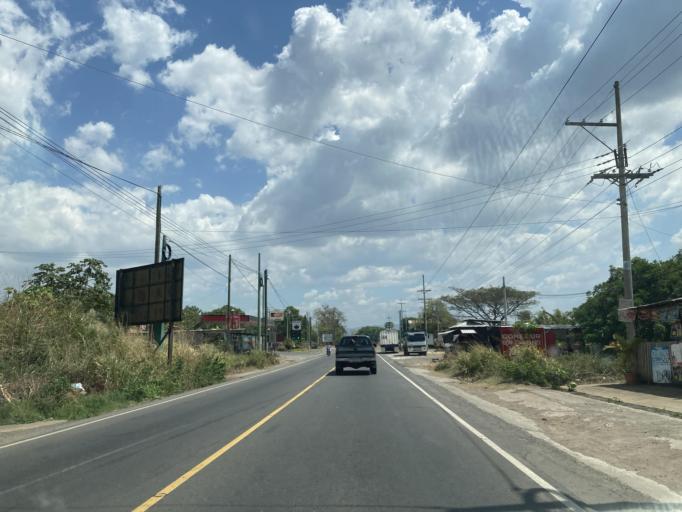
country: GT
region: Santa Rosa
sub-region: Municipio de Chiquimulilla
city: Chiquimulilla
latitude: 14.0677
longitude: -90.3941
